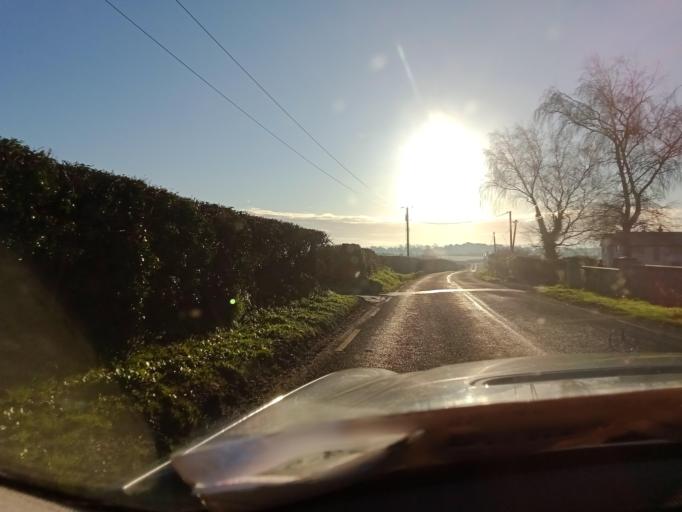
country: IE
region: Leinster
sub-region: Kilkenny
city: Callan
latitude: 52.5360
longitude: -7.3880
